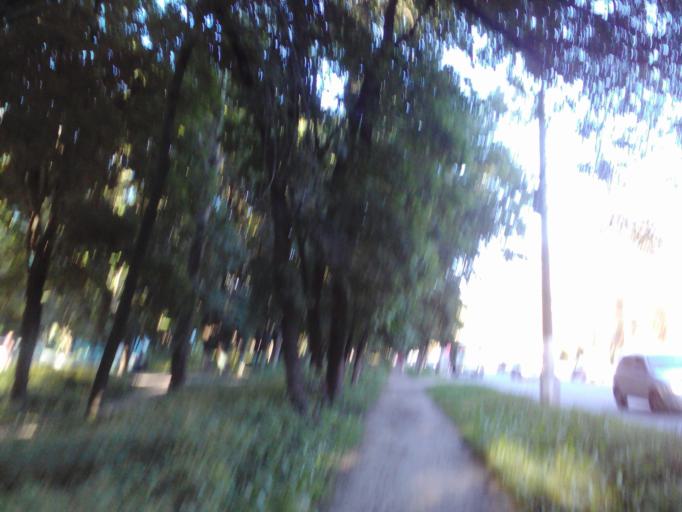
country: RU
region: Kursk
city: Voroshnevo
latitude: 51.6682
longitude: 36.0879
